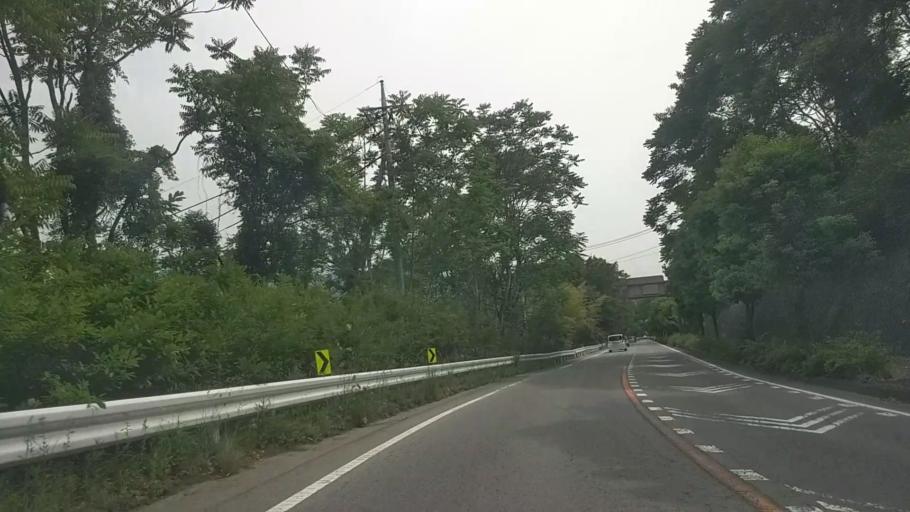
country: JP
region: Yamanashi
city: Isawa
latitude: 35.5920
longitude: 138.5900
